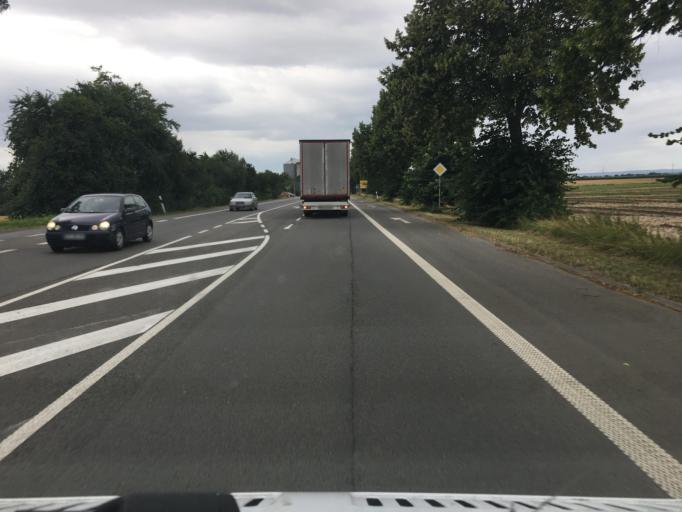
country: DE
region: North Rhine-Westphalia
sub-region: Regierungsbezirk Koln
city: Norvenich
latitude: 50.8139
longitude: 6.6344
